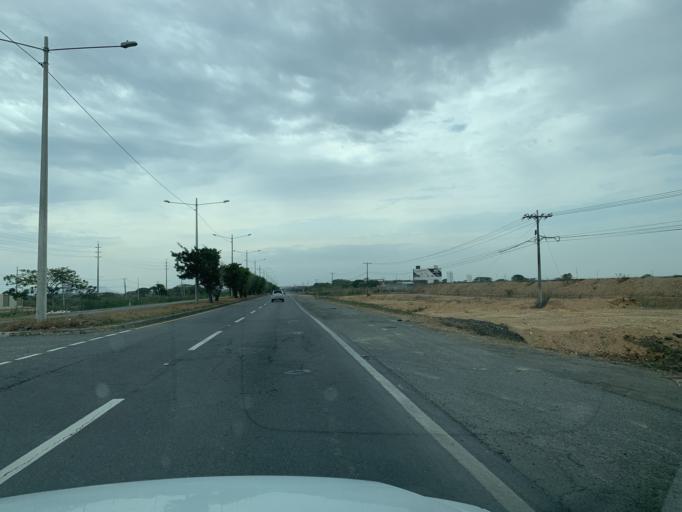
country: EC
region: Guayas
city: Eloy Alfaro
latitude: -2.1935
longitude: -79.7910
